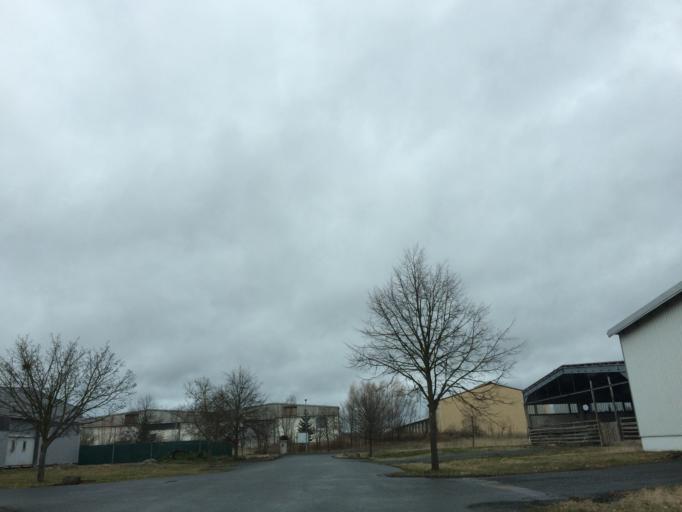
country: DE
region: Thuringia
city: Quaschwitz
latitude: 50.6805
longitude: 11.7177
